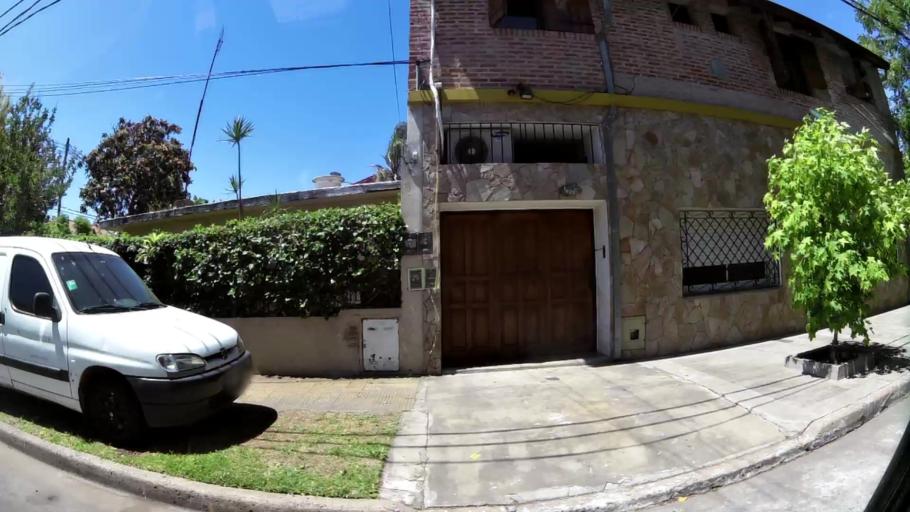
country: AR
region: Buenos Aires
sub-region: Partido de San Isidro
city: San Isidro
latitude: -34.5001
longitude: -58.5314
